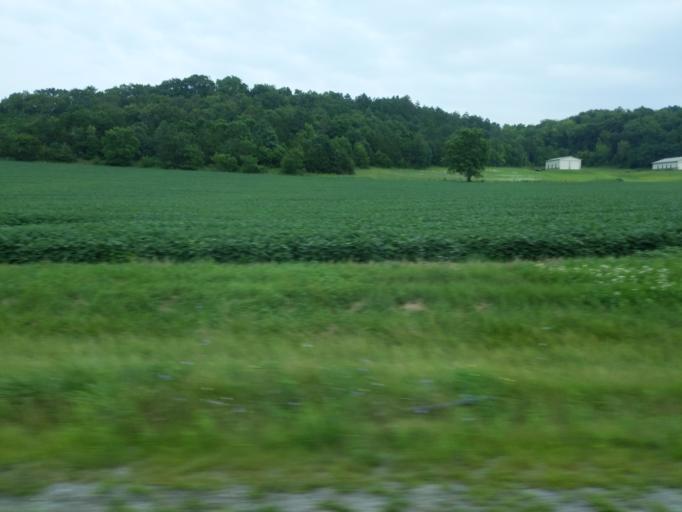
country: US
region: Wisconsin
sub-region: Dane County
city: Mazomanie
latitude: 43.1878
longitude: -89.7591
